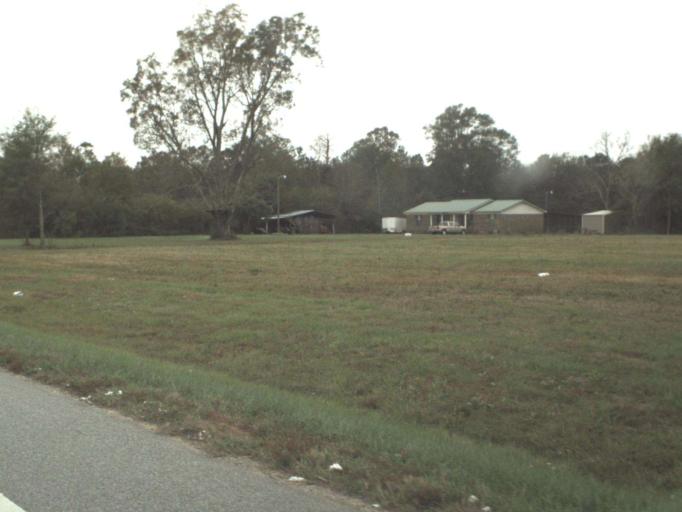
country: US
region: Alabama
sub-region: Escambia County
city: Atmore
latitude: 30.9555
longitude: -87.4863
